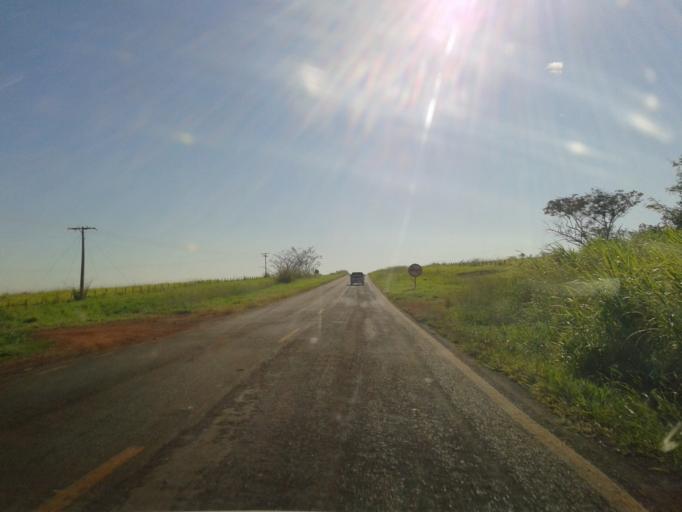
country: BR
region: Minas Gerais
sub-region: Capinopolis
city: Capinopolis
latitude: -18.6238
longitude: -49.5354
